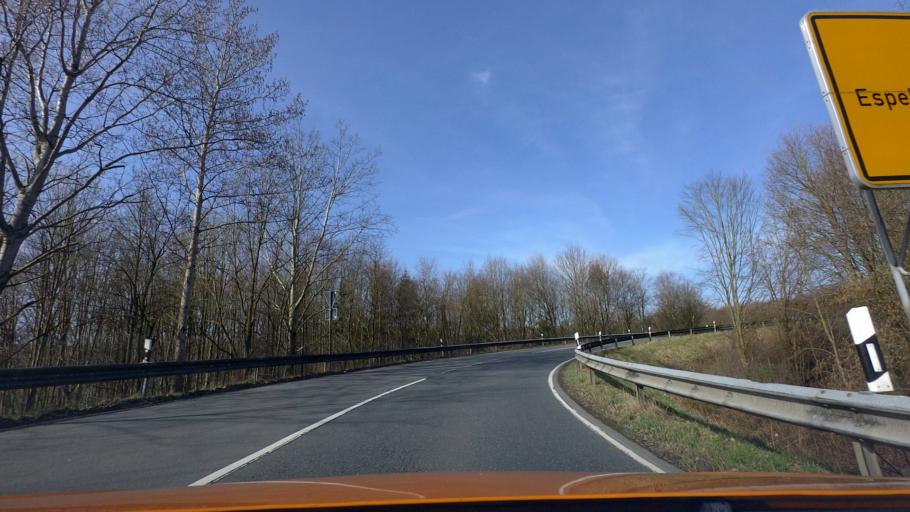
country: DE
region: North Rhine-Westphalia
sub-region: Regierungsbezirk Detmold
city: Petershagen
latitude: 52.3792
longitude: 8.9527
